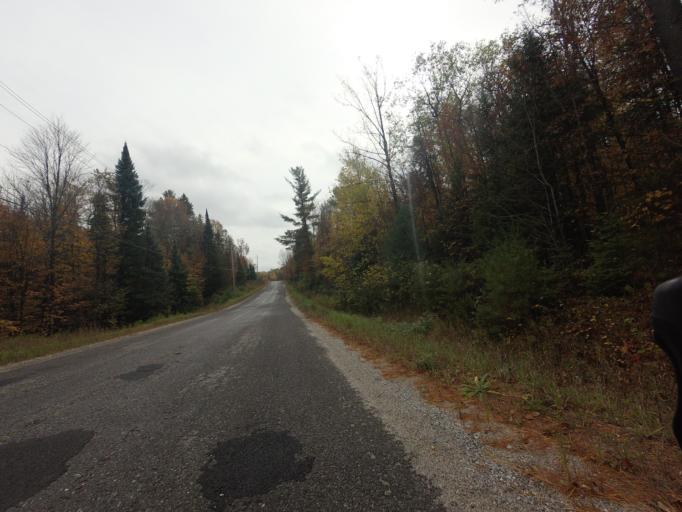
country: CA
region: Ontario
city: Perth
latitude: 45.1169
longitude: -76.5143
